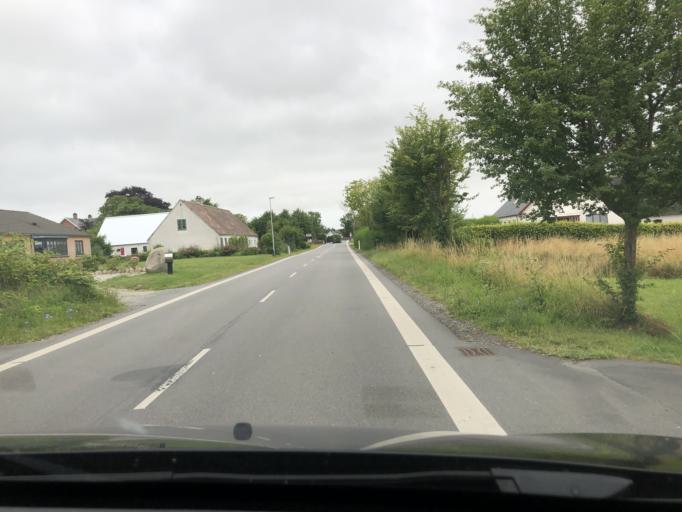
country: DK
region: South Denmark
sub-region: AEro Kommune
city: Marstal
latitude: 54.8552
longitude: 10.5018
